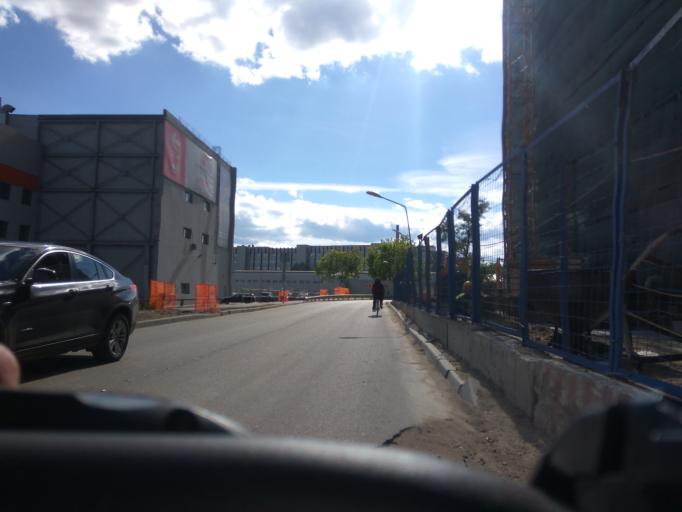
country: RU
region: Moscow
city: Mar'ina Roshcha
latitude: 55.8023
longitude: 37.5924
